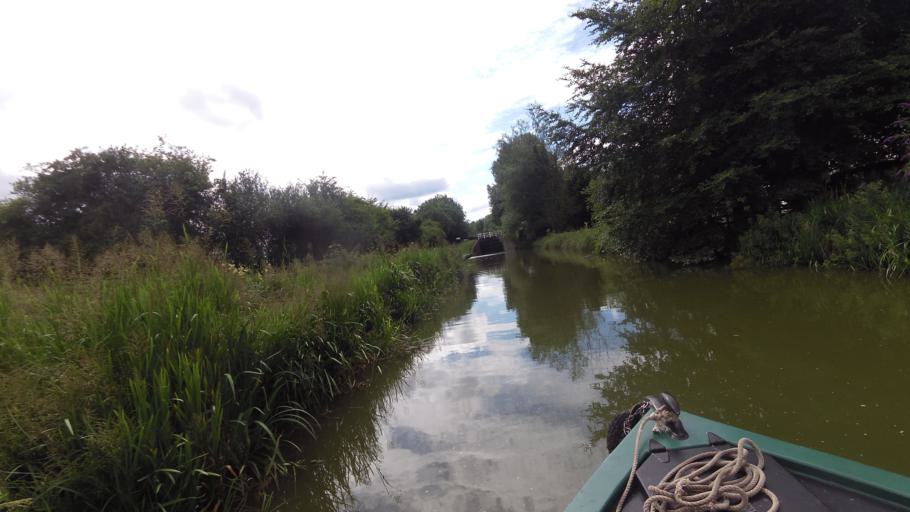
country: GB
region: England
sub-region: Wiltshire
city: Chilton Foliat
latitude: 51.4144
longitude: -1.5379
